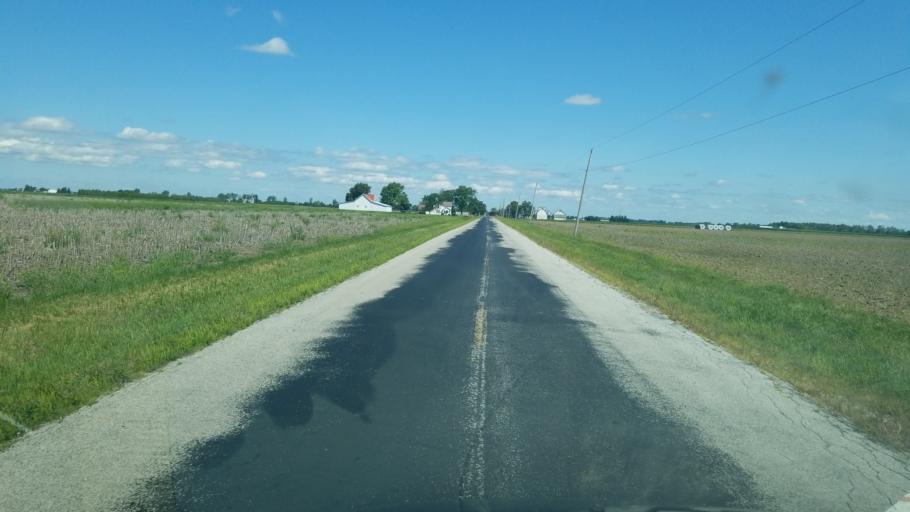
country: US
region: Ohio
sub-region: Henry County
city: Deshler
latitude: 41.2564
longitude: -83.8432
